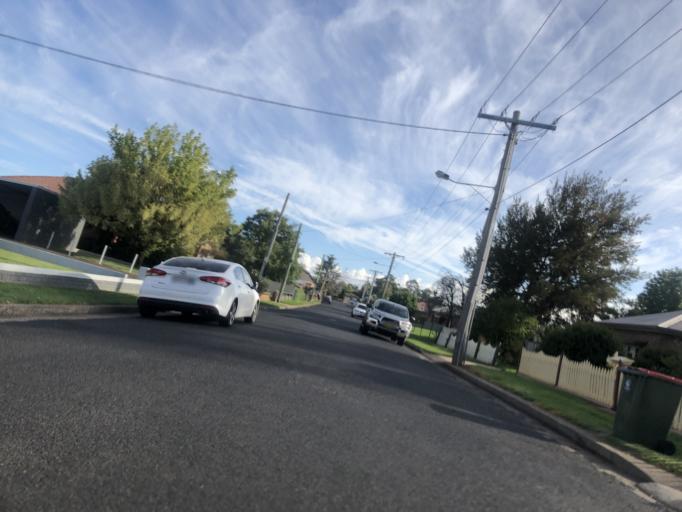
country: AU
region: New South Wales
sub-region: Orange Municipality
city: Orange
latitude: -33.2794
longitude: 149.1033
